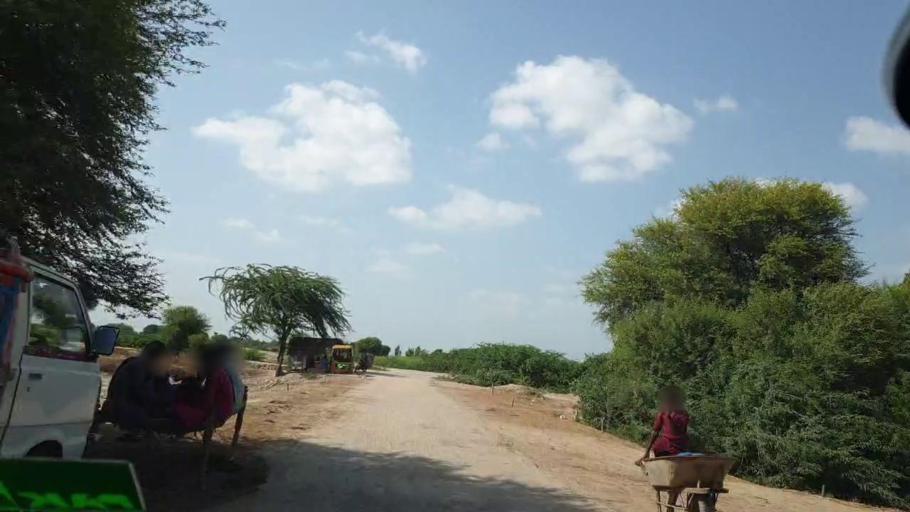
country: PK
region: Sindh
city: Naukot
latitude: 24.6502
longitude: 69.2195
